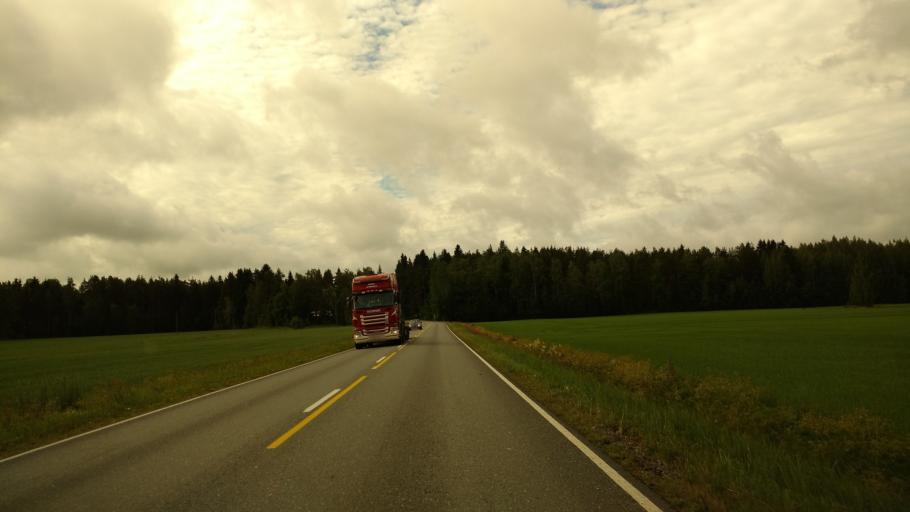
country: FI
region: Varsinais-Suomi
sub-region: Loimaa
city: Koski Tl
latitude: 60.6332
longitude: 23.1052
